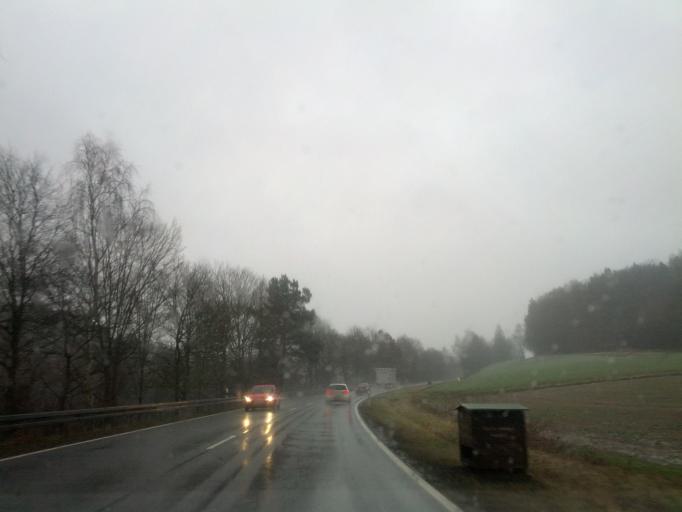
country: DE
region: Thuringia
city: Gerstungen
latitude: 51.0255
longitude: 10.0246
